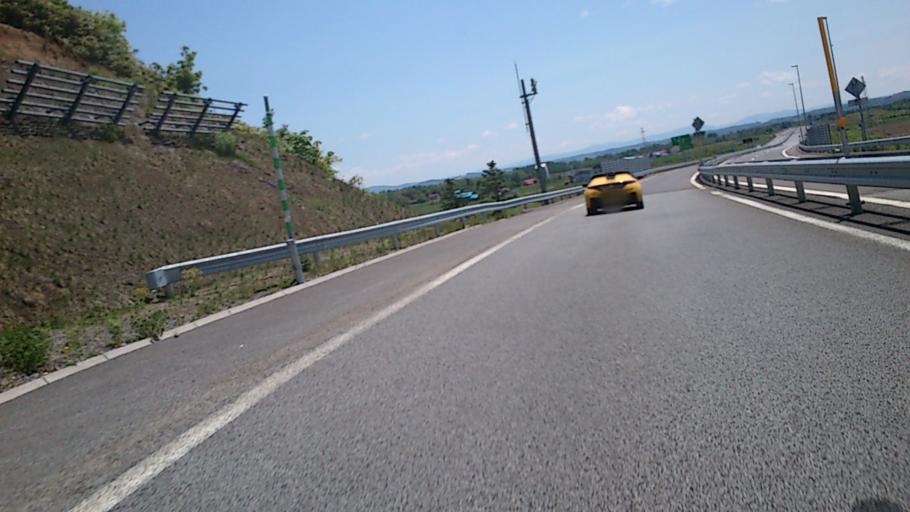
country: JP
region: Hokkaido
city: Nayoro
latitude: 44.4826
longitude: 142.3660
